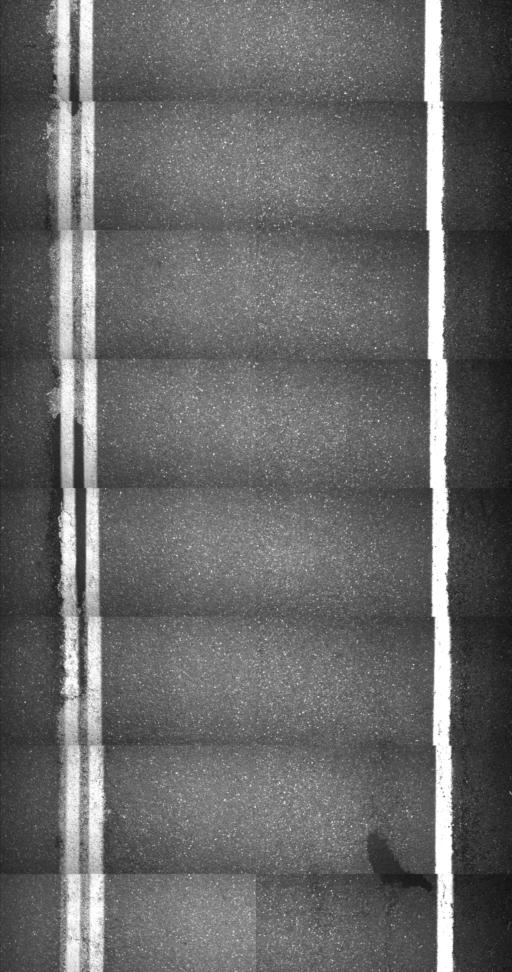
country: US
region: Massachusetts
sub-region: Franklin County
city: Colrain
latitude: 42.7420
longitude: -72.7326
